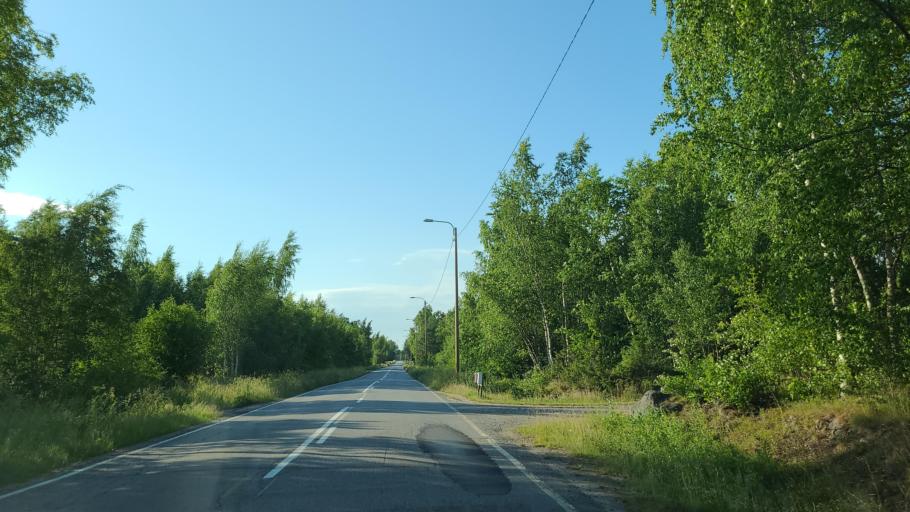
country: FI
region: Ostrobothnia
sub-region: Vaasa
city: Replot
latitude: 63.3307
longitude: 21.3378
